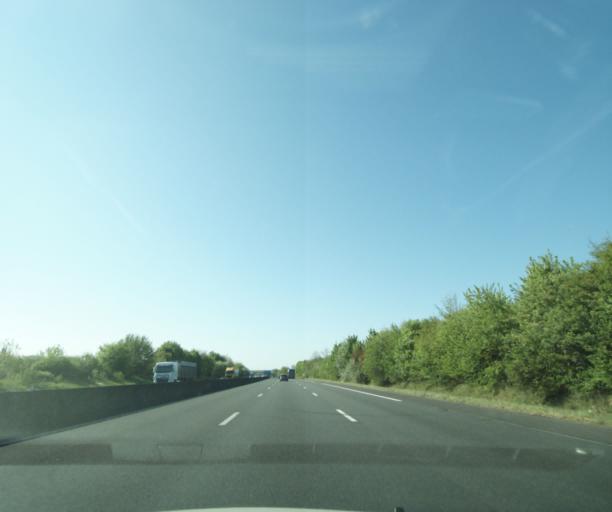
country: FR
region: Centre
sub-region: Departement du Loiret
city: Saran
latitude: 47.9584
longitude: 1.8521
